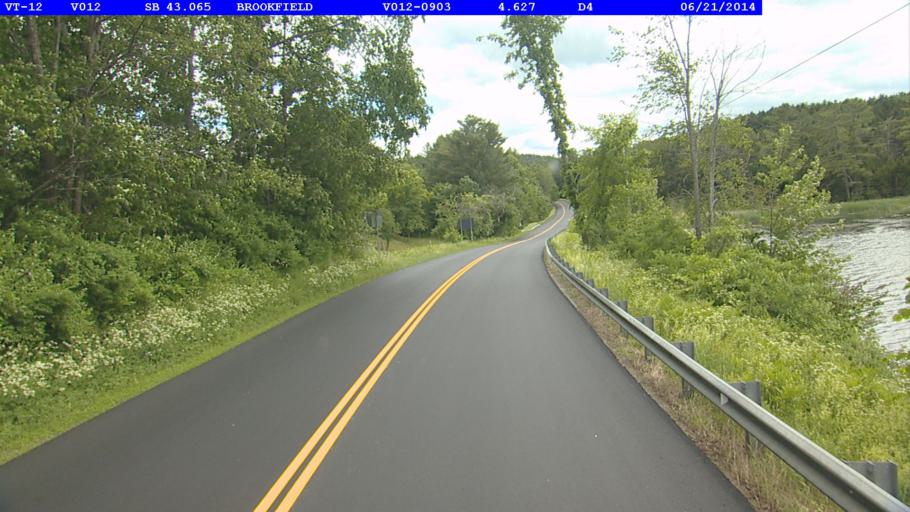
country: US
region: Vermont
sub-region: Washington County
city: Northfield
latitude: 44.0667
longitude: -72.6330
